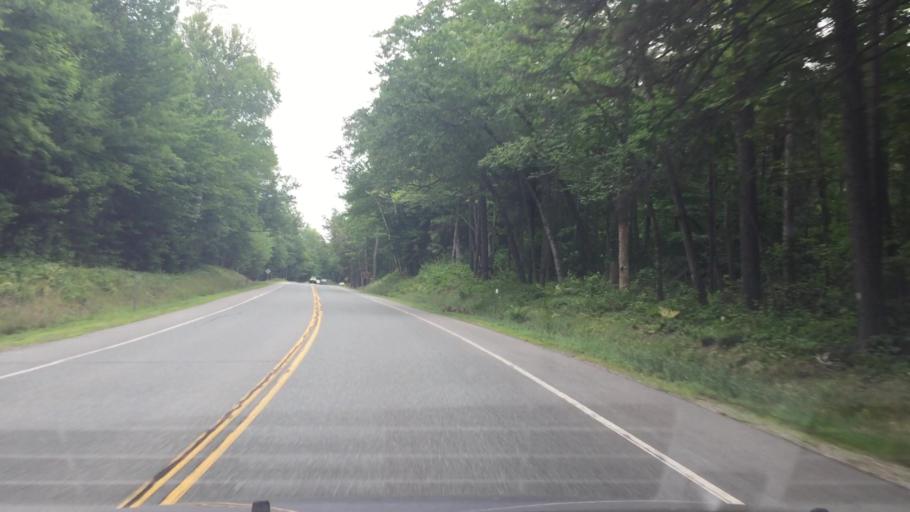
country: US
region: New Hampshire
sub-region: Grafton County
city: Deerfield
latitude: 44.2369
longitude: -71.6597
